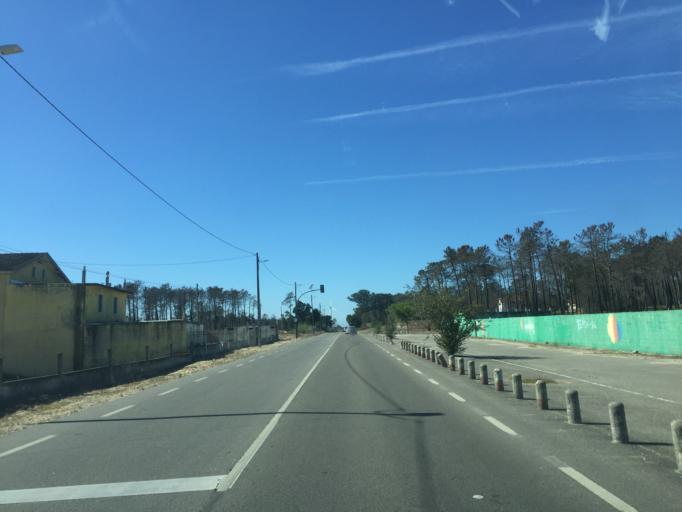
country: PT
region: Coimbra
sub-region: Mira
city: Mira
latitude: 40.3216
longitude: -8.7811
